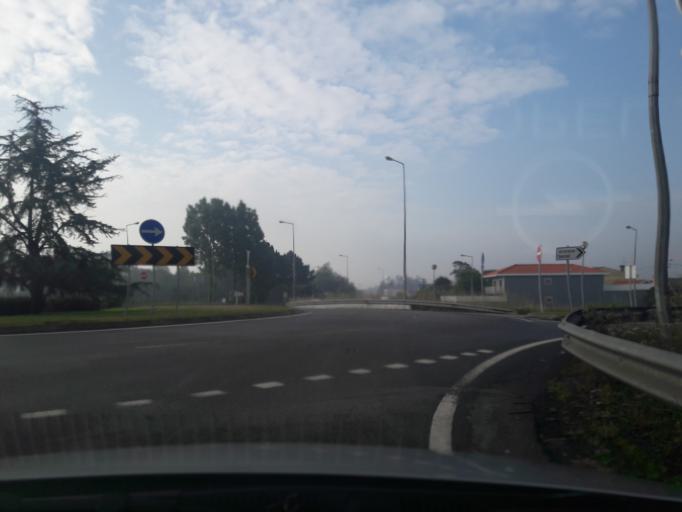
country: PT
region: Porto
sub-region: Vila do Conde
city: Arvore
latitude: 41.3193
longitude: -8.7117
